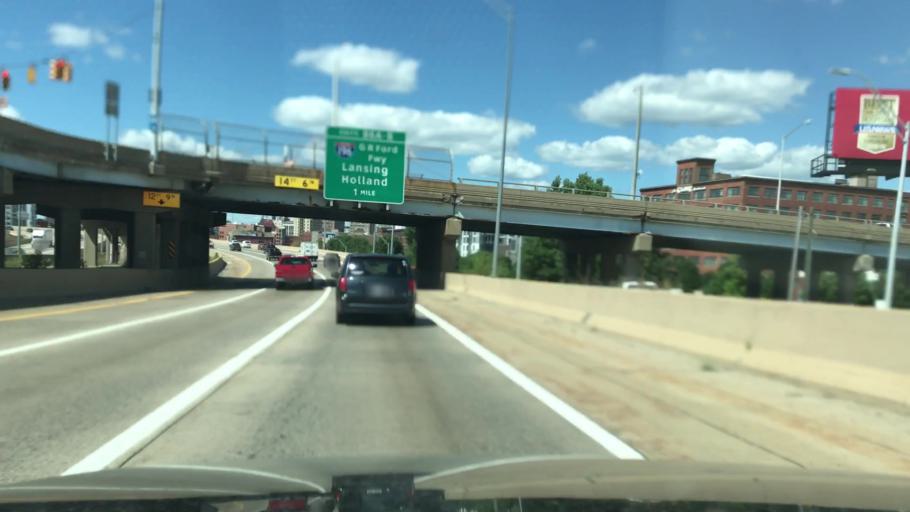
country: US
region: Michigan
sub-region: Kent County
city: Grand Rapids
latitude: 42.9557
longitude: -85.6713
